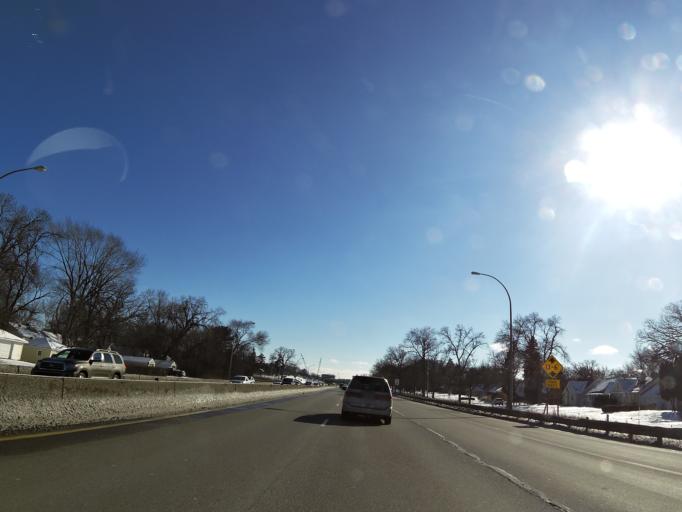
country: US
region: Minnesota
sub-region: Hennepin County
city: Saint Louis Park
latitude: 44.9538
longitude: -93.3480
